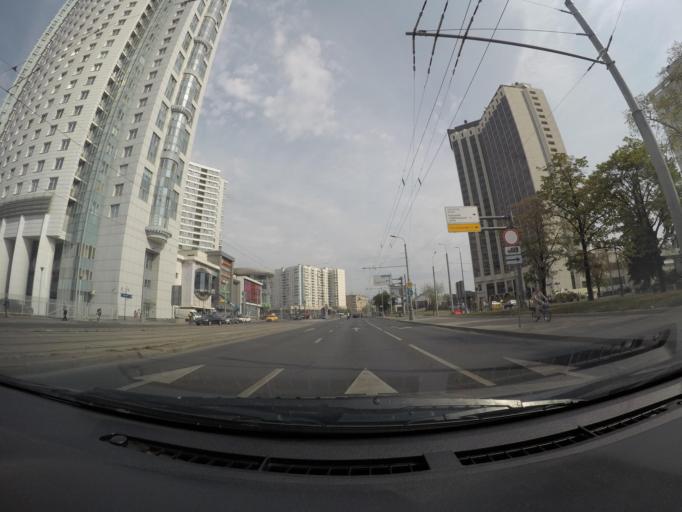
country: RU
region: Moscow
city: Sokol'niki
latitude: 55.7875
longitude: 37.6787
